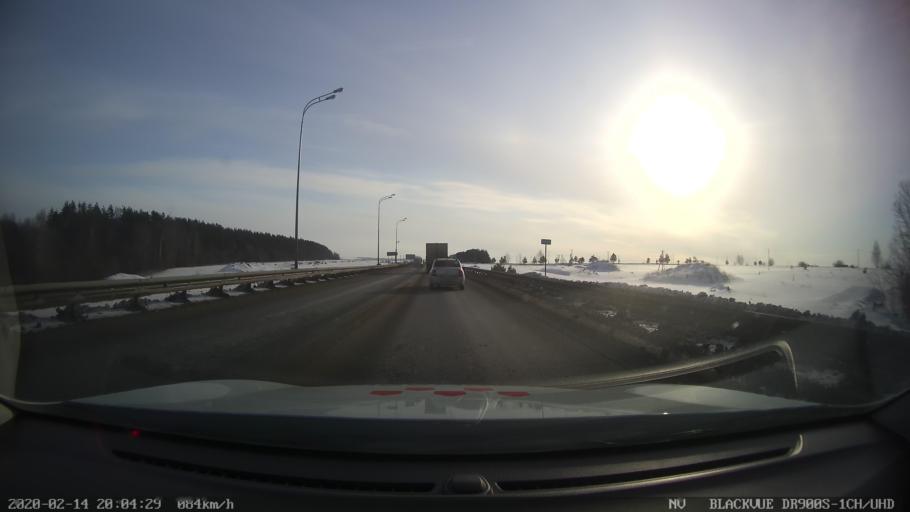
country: RU
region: Tatarstan
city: Sviyazhsk
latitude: 55.7342
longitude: 48.7909
